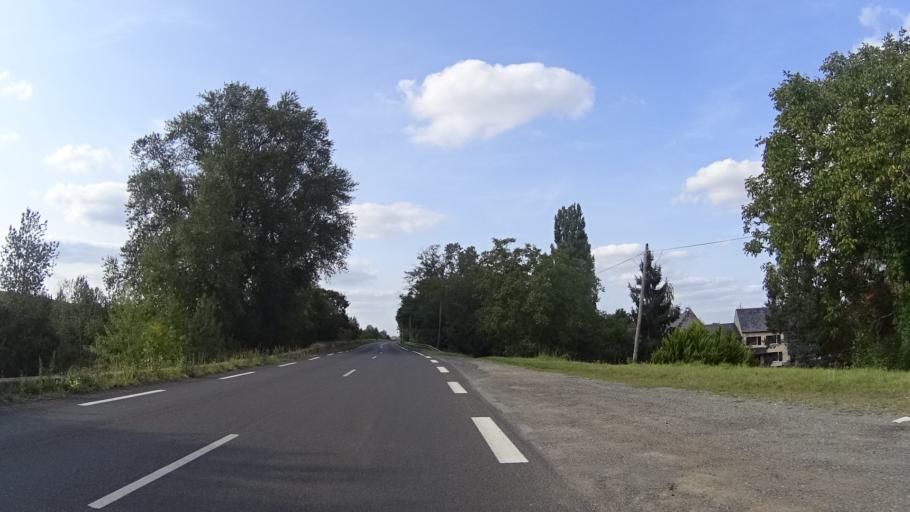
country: FR
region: Pays de la Loire
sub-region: Departement de Maine-et-Loire
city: La Menitre
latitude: 47.3751
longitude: -0.2588
